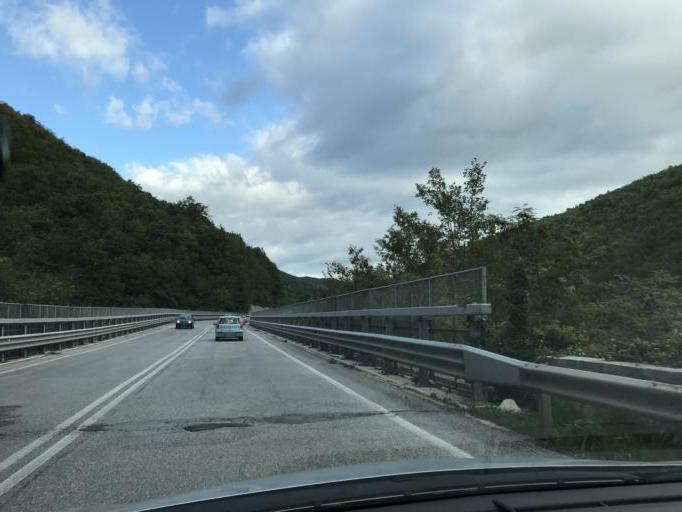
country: IT
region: Umbria
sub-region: Provincia di Perugia
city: Spoleto
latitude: 42.6846
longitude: 12.7263
